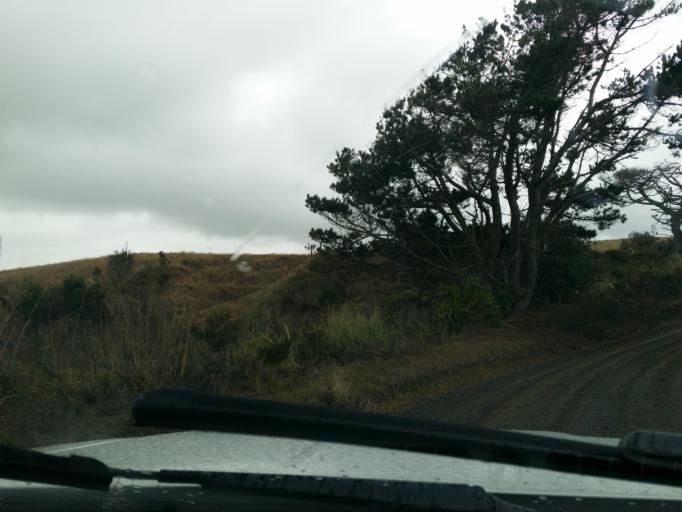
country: NZ
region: Northland
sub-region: Kaipara District
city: Dargaville
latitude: -35.9997
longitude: 173.7949
